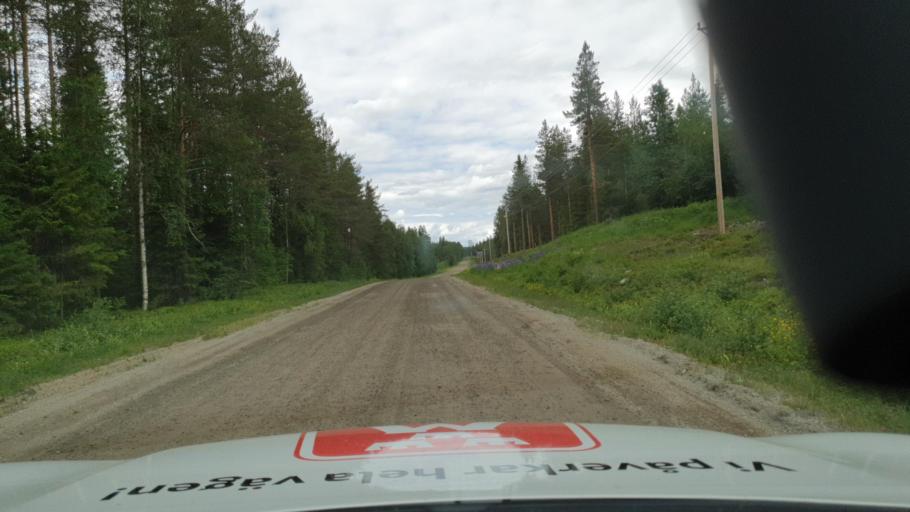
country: SE
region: Vaesterbotten
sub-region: Bjurholms Kommun
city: Bjurholm
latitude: 63.8504
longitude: 18.9834
